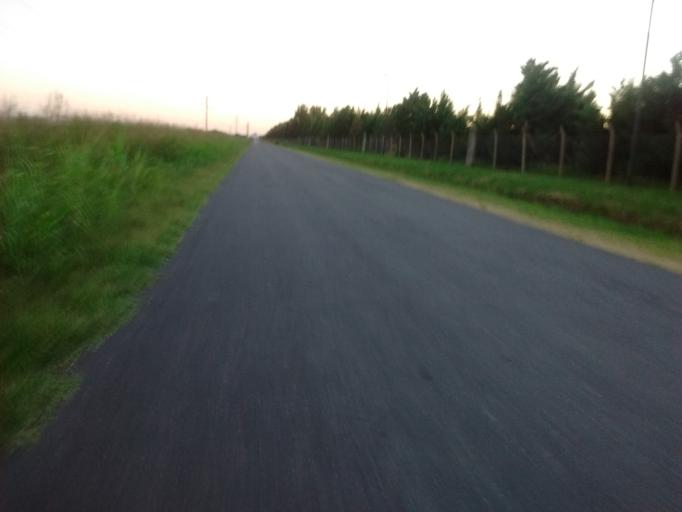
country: AR
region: Santa Fe
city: Funes
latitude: -32.9455
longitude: -60.8196
